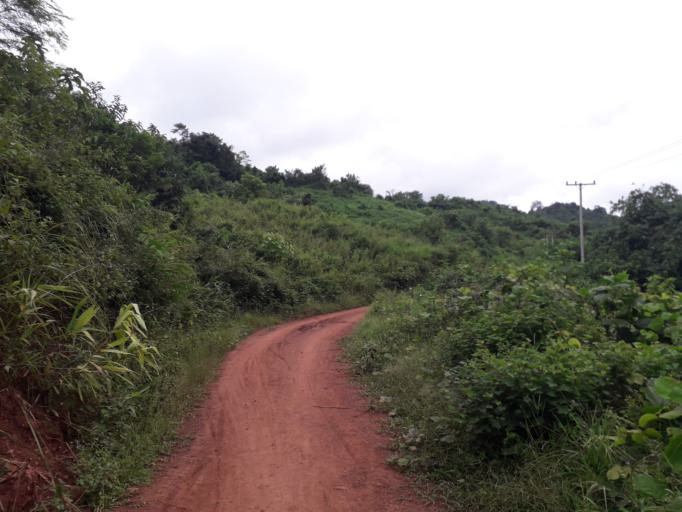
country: CN
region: Yunnan
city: Menglie
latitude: 22.2125
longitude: 101.6585
